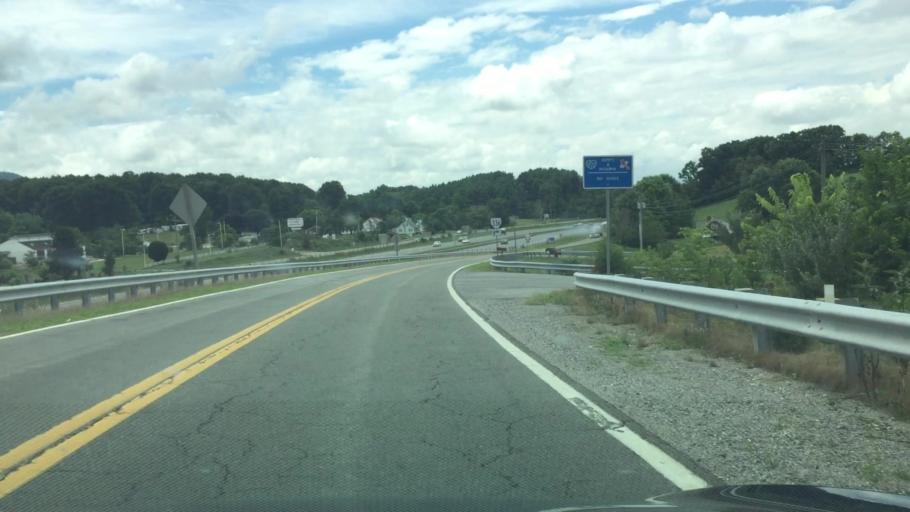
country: US
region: Virginia
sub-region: Wythe County
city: Wytheville
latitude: 36.9380
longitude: -80.9960
